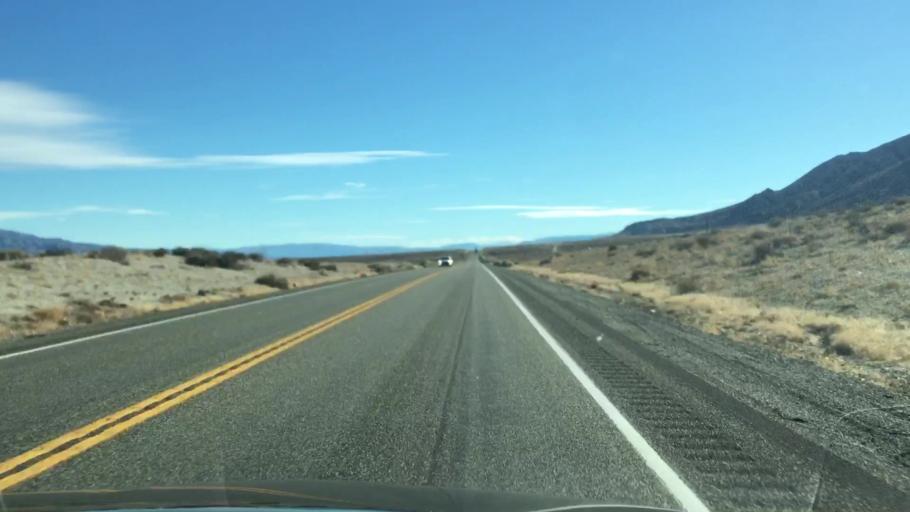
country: US
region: Nevada
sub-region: Mineral County
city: Hawthorne
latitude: 38.8156
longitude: -118.7669
